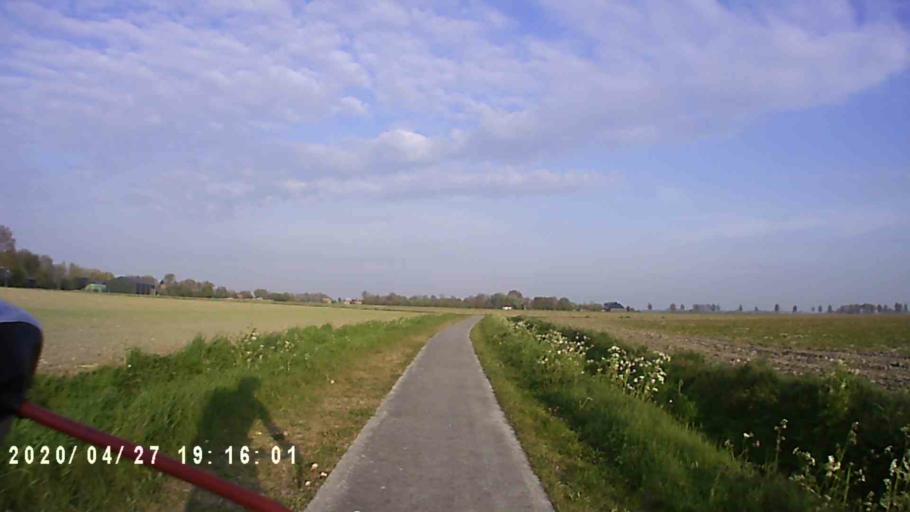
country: NL
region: Groningen
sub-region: Gemeente Winsum
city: Winsum
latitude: 53.4047
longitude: 6.4662
